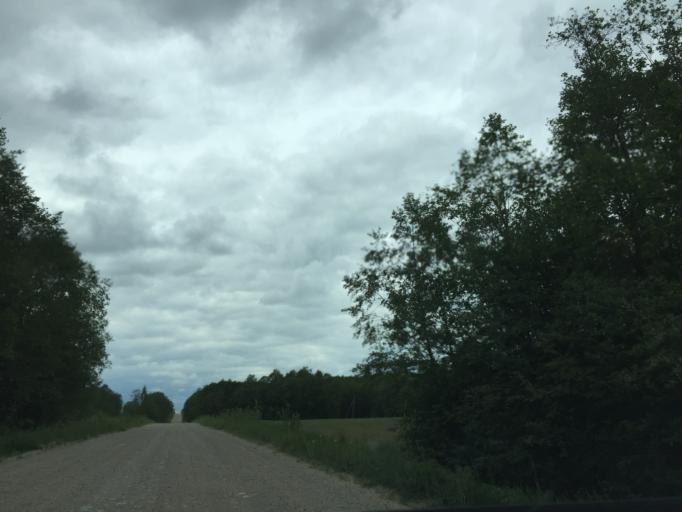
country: LV
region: Dagda
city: Dagda
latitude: 55.9988
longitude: 27.6089
